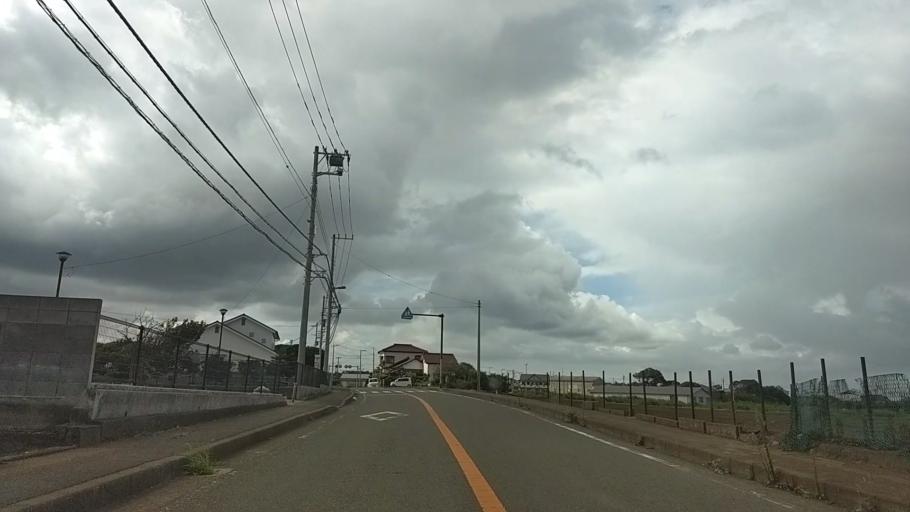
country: JP
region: Kanagawa
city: Miura
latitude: 35.1474
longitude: 139.6696
